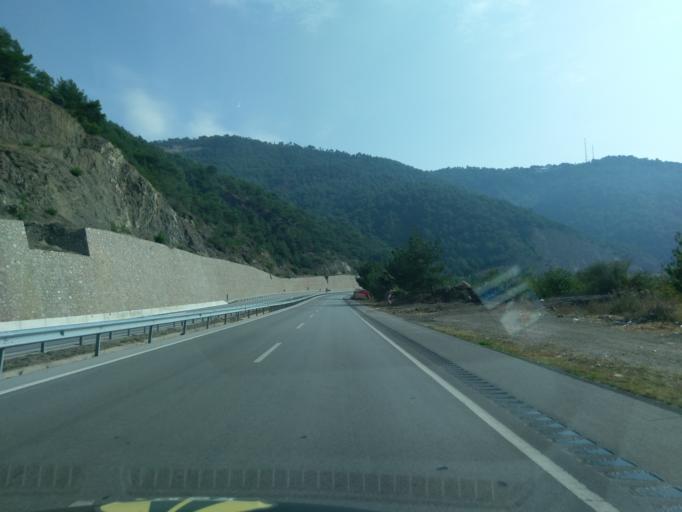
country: TR
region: Amasya
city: Akdag
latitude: 40.7530
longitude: 36.0818
